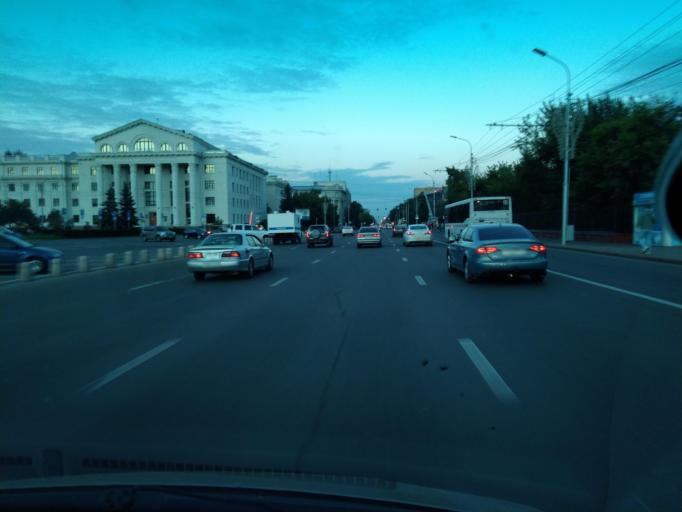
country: RU
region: Krasnoyarskiy
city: Krasnoyarsk
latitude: 56.0096
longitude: 92.8532
